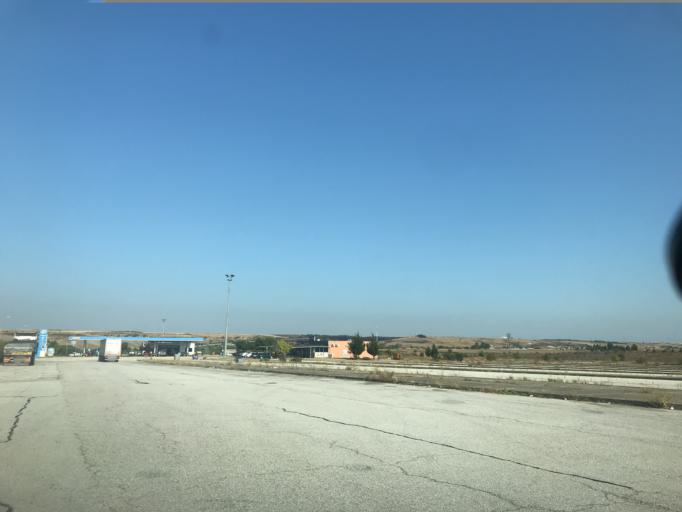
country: TR
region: Kirklareli
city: Babaeski
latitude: 41.5234
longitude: 27.0851
